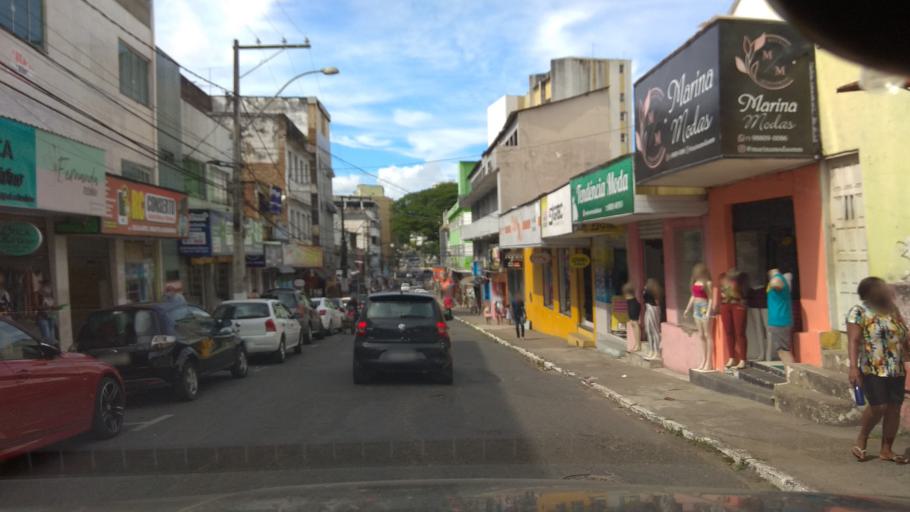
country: BR
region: Bahia
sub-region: Itabuna
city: Itabuna
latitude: -14.7915
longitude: -39.2764
